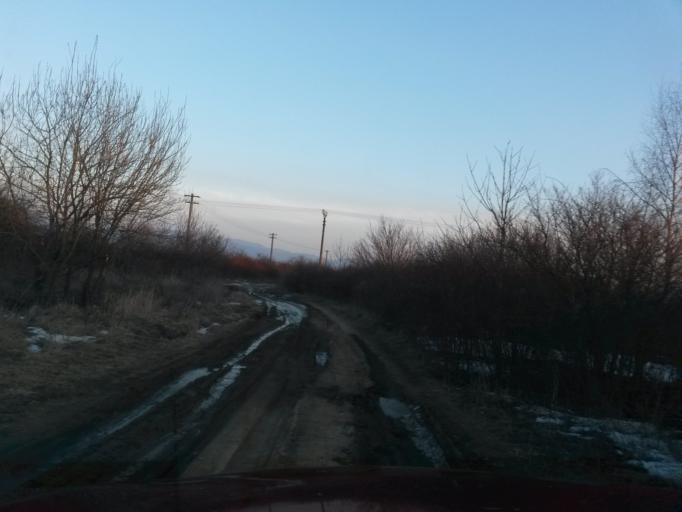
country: SK
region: Kosicky
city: Kosice
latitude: 48.7267
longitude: 21.2191
